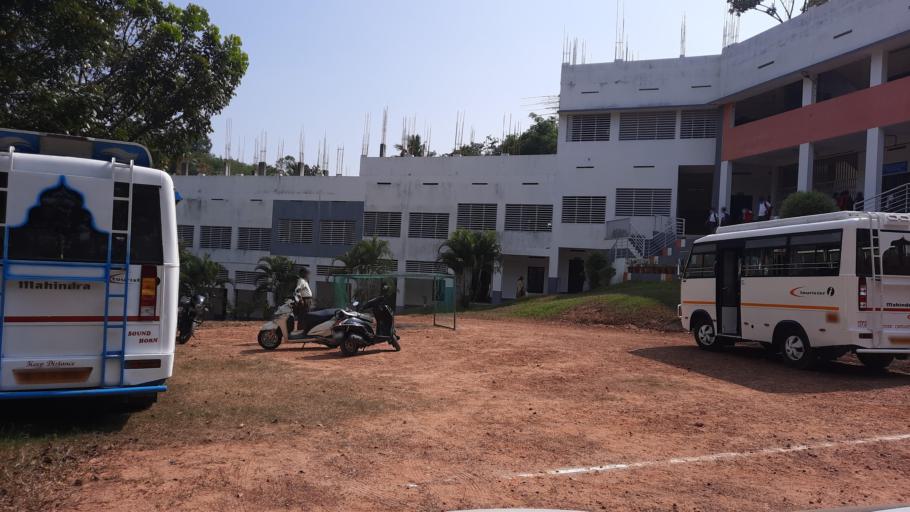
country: IN
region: Kerala
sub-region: Thiruvananthapuram
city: Nedumangad
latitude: 8.5954
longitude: 76.9264
